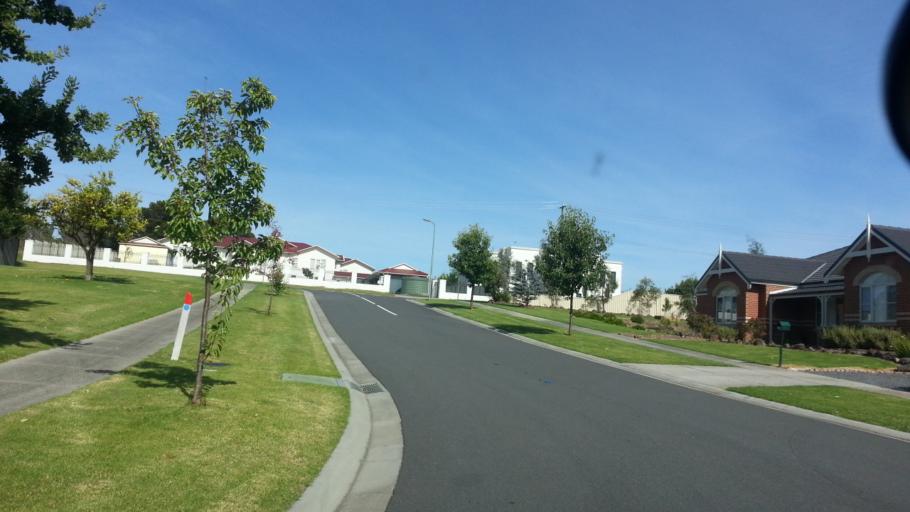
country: AU
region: Victoria
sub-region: Casey
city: Endeavour Hills
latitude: -37.9764
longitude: 145.2869
